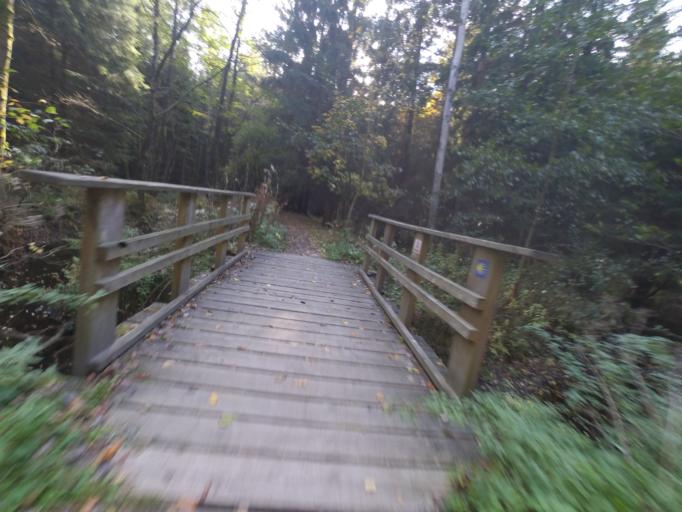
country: DE
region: Saxony
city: Radeberg
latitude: 51.0920
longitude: 13.8611
